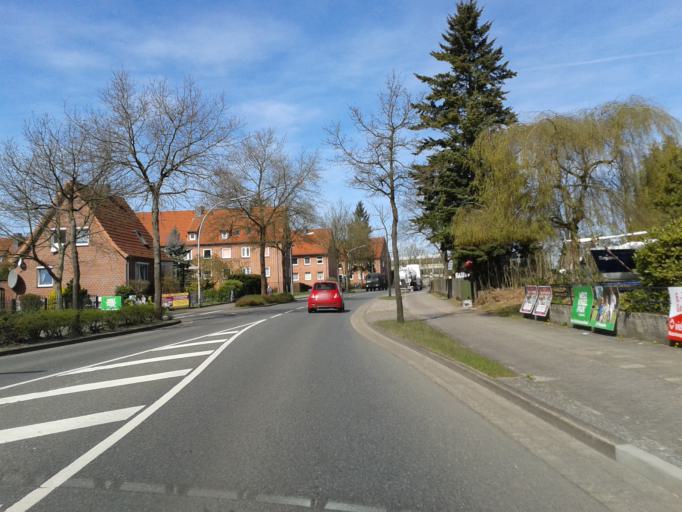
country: DE
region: Lower Saxony
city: Munster
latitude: 52.9814
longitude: 10.0892
